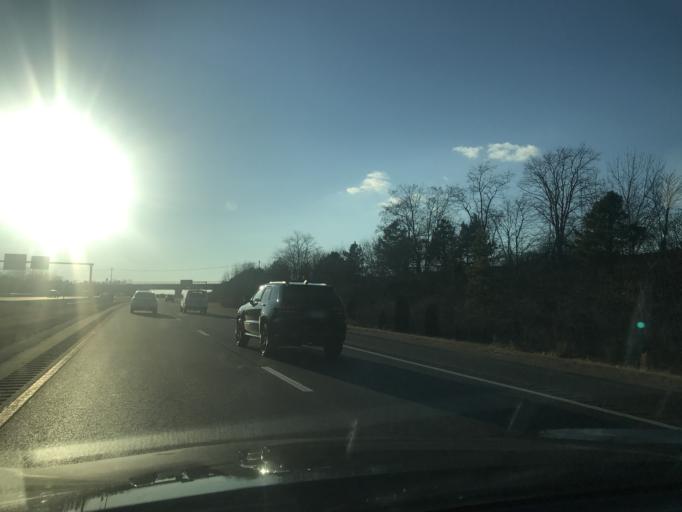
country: US
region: Massachusetts
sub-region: Plymouth County
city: North Plymouth
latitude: 41.9614
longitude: -70.7059
